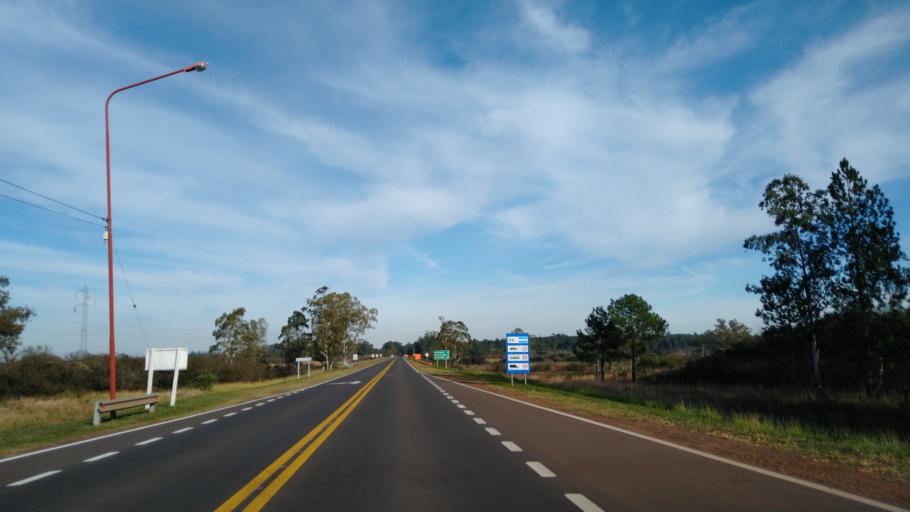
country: AR
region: Corrientes
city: Yapeyu
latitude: -29.4224
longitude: -56.8471
